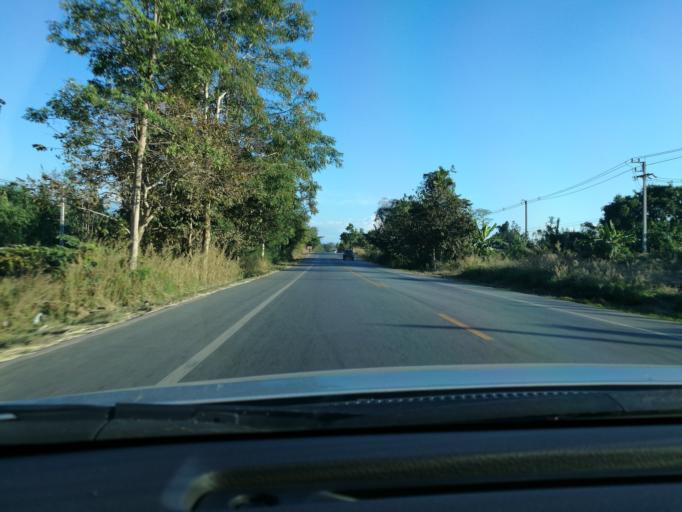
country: TH
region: Phitsanulok
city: Nakhon Thai
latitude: 17.0415
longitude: 100.8122
